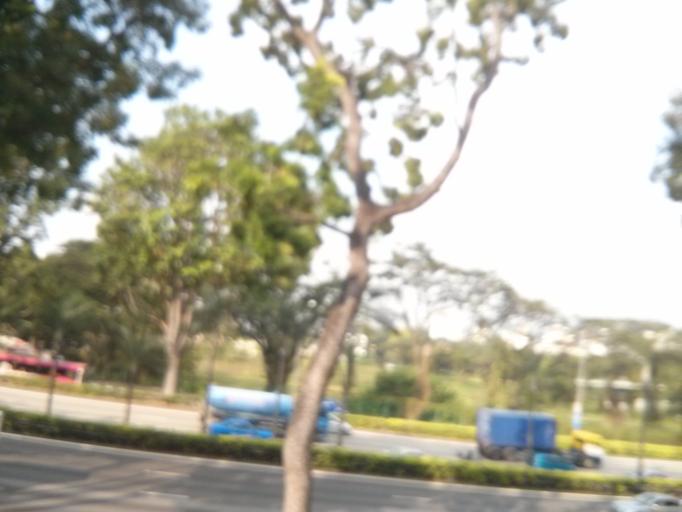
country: SG
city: Singapore
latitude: 1.2895
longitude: 103.7921
